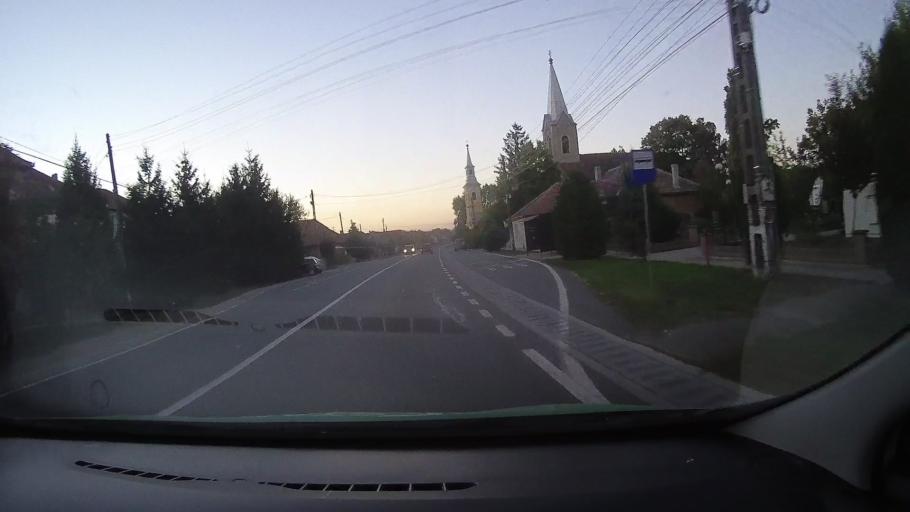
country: RO
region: Bihor
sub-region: Comuna Tarcea
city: Tarcea
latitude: 47.4569
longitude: 22.1732
